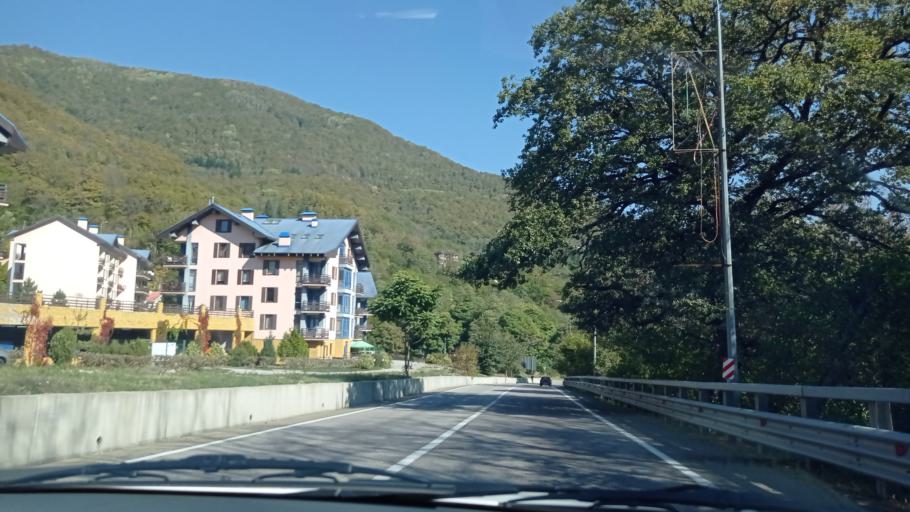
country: RU
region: Krasnodarskiy
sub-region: Sochi City
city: Krasnaya Polyana
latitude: 43.6842
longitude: 40.2268
